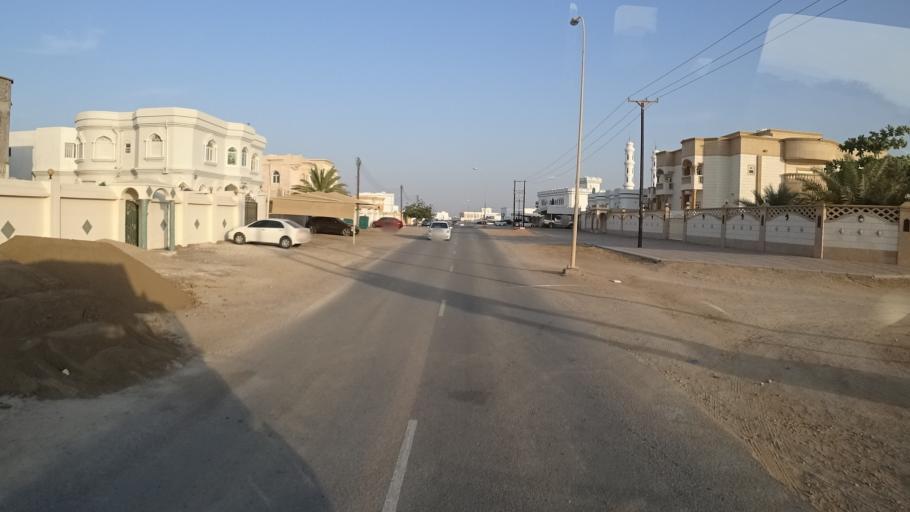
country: OM
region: Ash Sharqiyah
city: Sur
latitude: 22.6132
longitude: 59.4640
